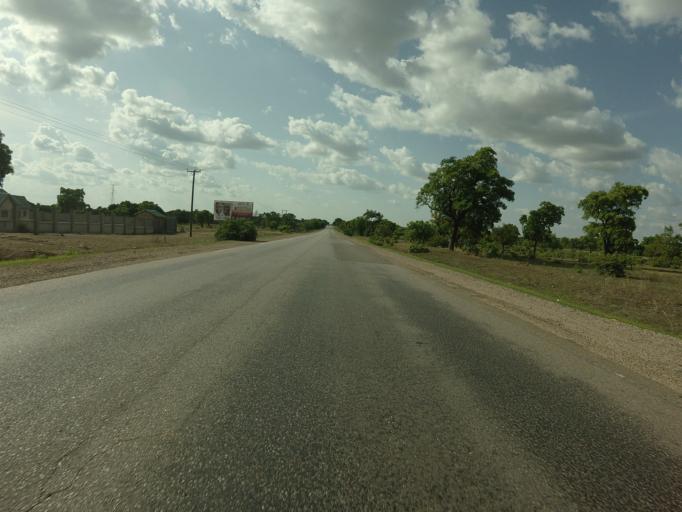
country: GH
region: Upper East
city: Bolgatanga
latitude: 10.6550
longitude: -0.8585
